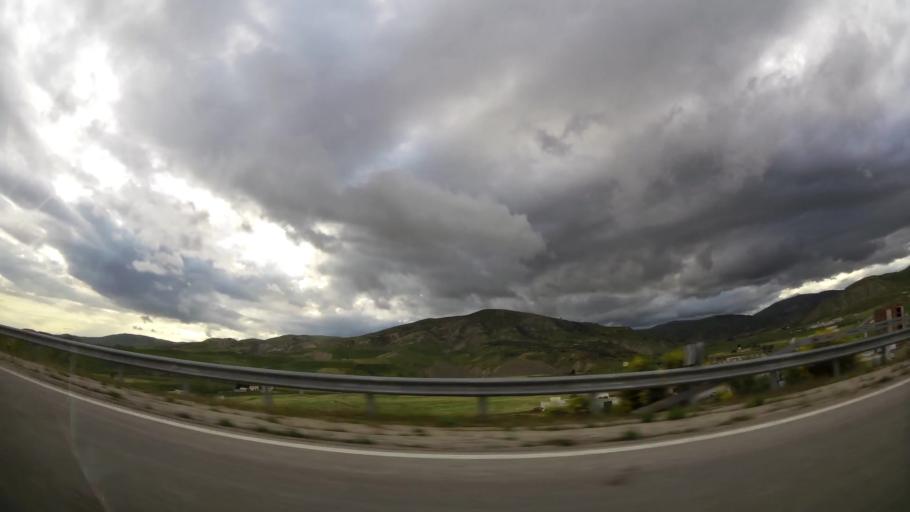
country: MA
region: Taza-Al Hoceima-Taounate
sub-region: Taza
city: Taza
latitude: 34.2639
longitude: -3.9564
